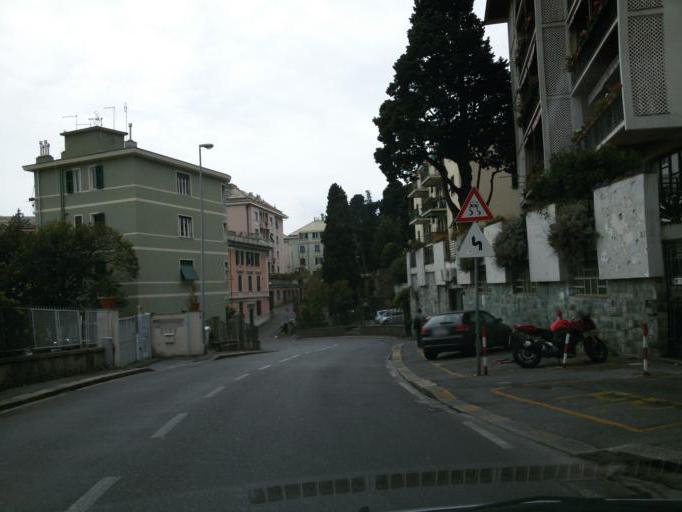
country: IT
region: Liguria
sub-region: Provincia di Genova
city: Genoa
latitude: 44.3996
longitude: 8.9789
